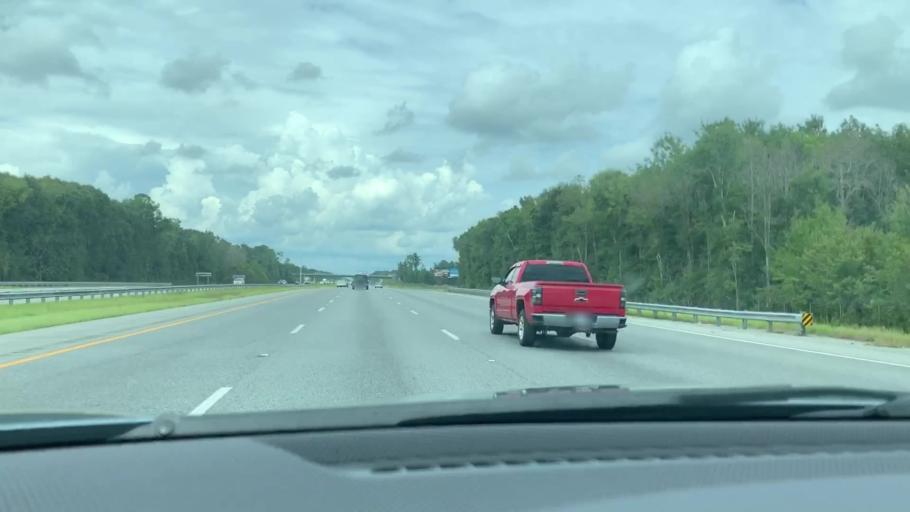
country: US
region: Georgia
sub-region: McIntosh County
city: Darien
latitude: 31.4870
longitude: -81.4469
